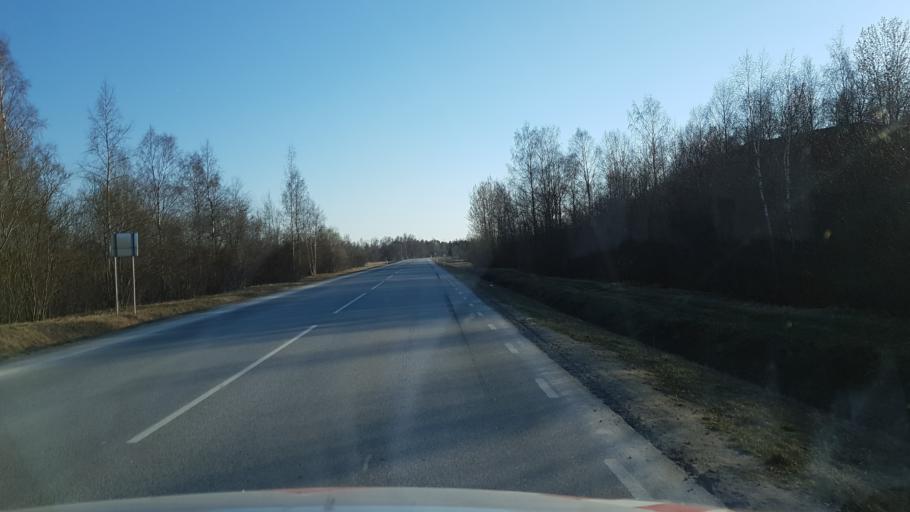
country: EE
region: Ida-Virumaa
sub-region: Kivioli linn
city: Kivioli
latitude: 59.3640
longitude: 26.9636
